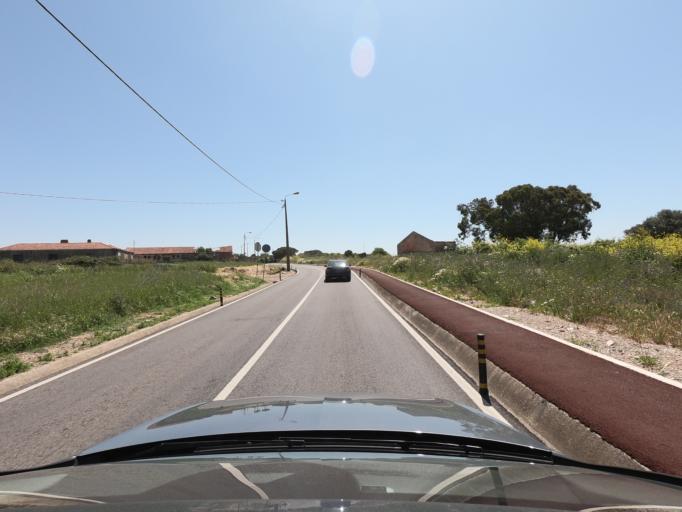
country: PT
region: Lisbon
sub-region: Cascais
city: Sao Domingos de Rana
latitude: 38.7334
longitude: -9.3505
